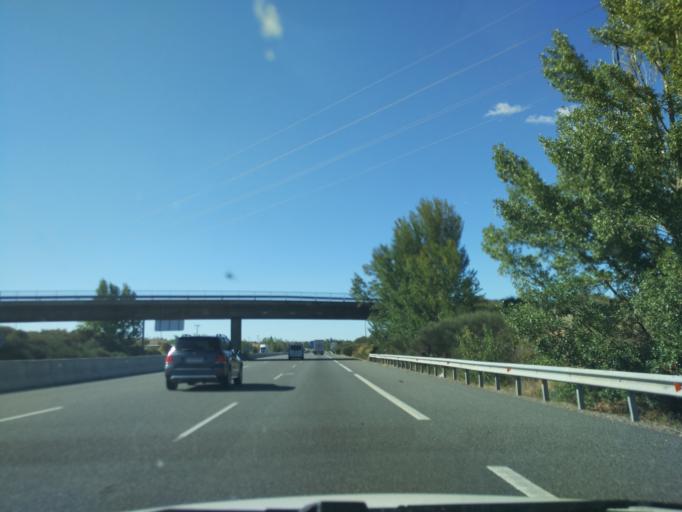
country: ES
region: Castille and Leon
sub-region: Provincia de Zamora
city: Benavente
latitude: 42.0076
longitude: -5.6616
